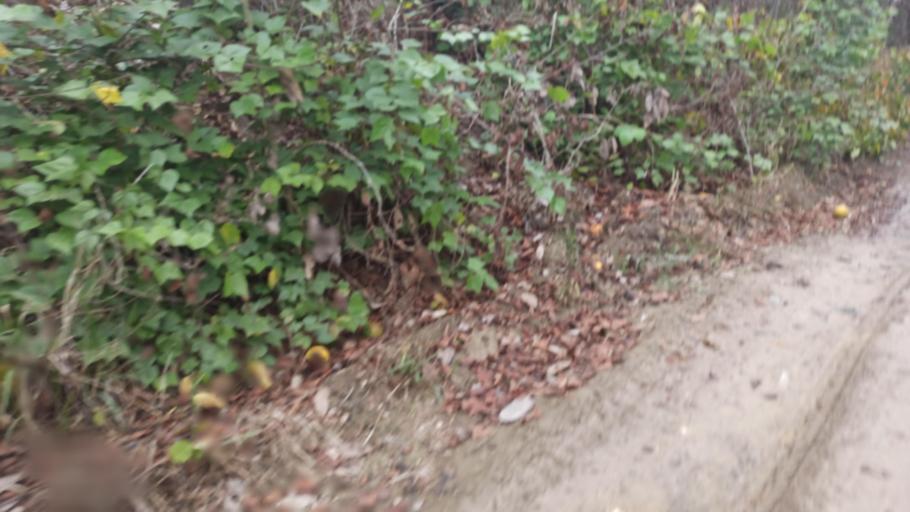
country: MX
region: Veracruz
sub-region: Papantla
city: El Chote
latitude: 20.3844
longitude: -97.3562
